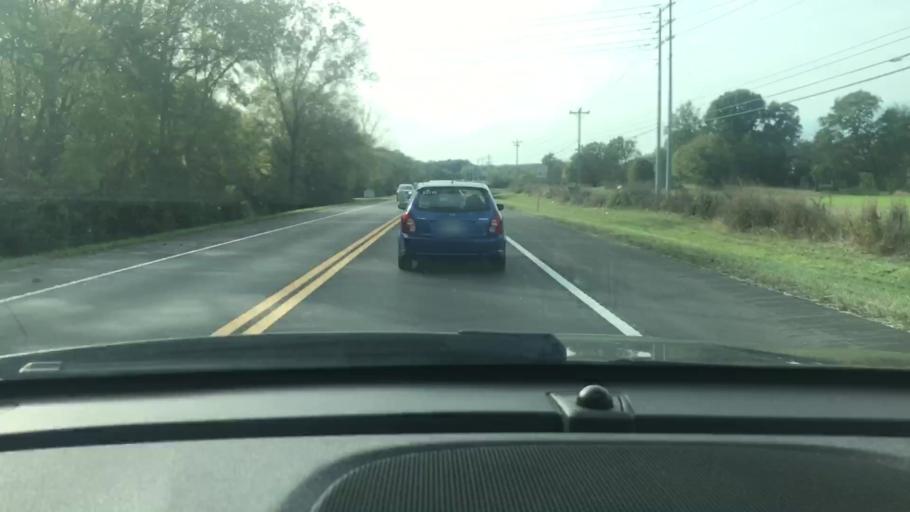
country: US
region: Tennessee
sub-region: Williamson County
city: Franklin
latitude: 35.9306
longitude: -86.9137
